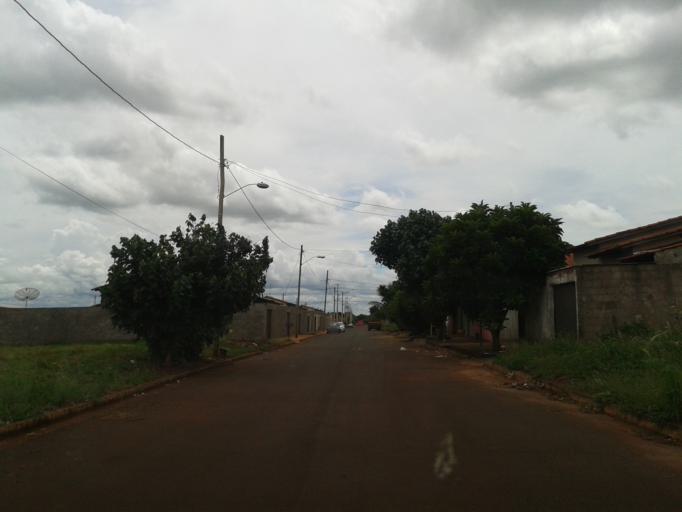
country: BR
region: Minas Gerais
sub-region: Centralina
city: Centralina
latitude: -18.5889
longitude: -49.2053
